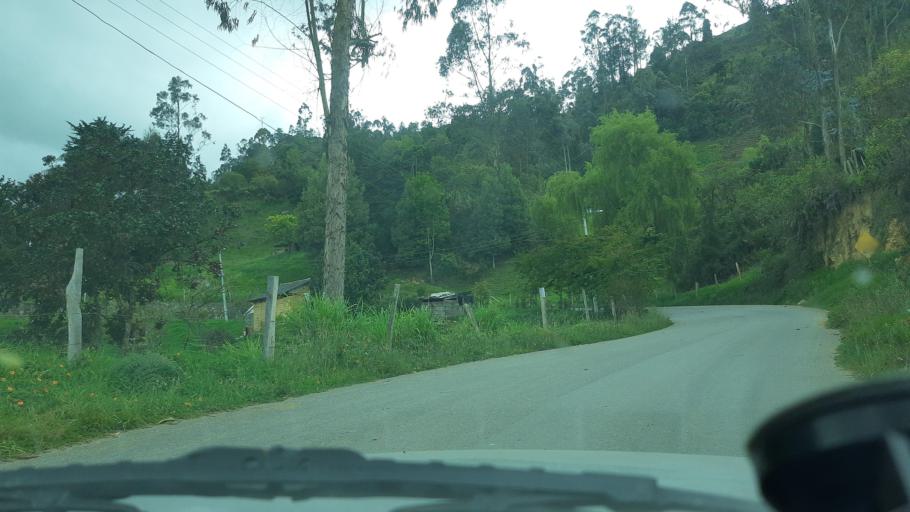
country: CO
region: Cundinamarca
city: Umbita
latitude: 5.2218
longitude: -73.4613
